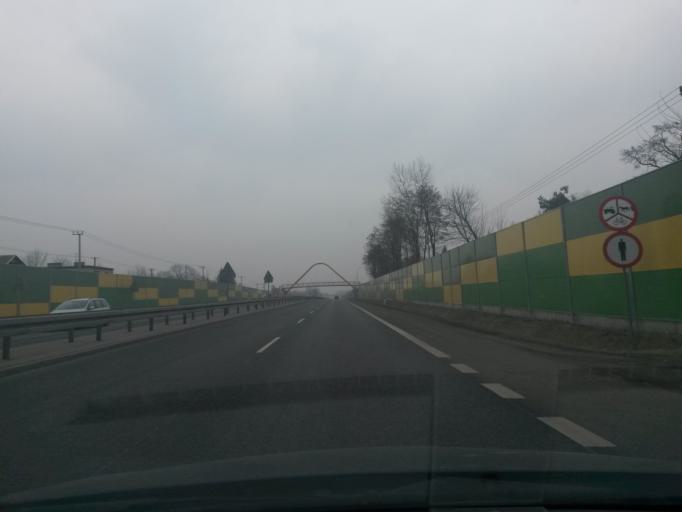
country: PL
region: Masovian Voivodeship
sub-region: Powiat legionowski
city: Bialobrzegi
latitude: 52.4751
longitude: 21.0322
